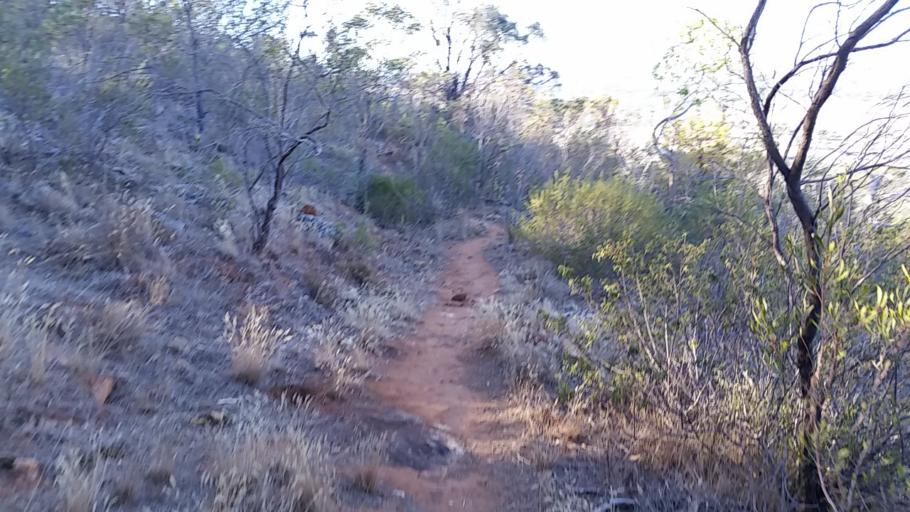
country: AU
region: South Australia
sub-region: Mount Barker
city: Nairne
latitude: -35.0632
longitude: 138.9219
